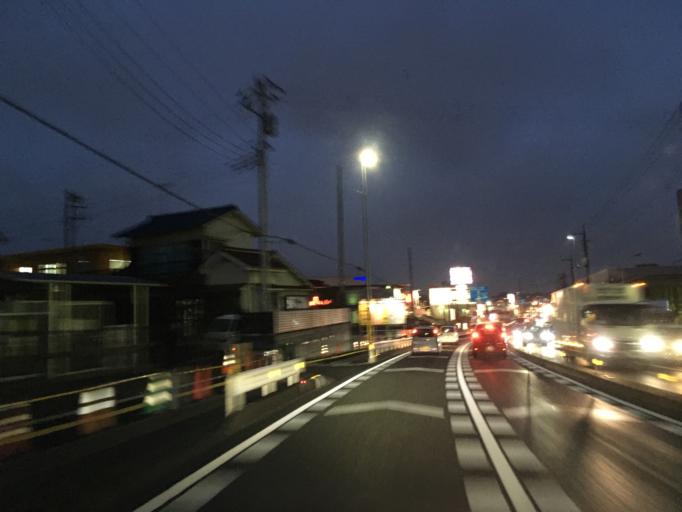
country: JP
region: Saitama
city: Shiki
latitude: 35.8058
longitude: 139.5512
